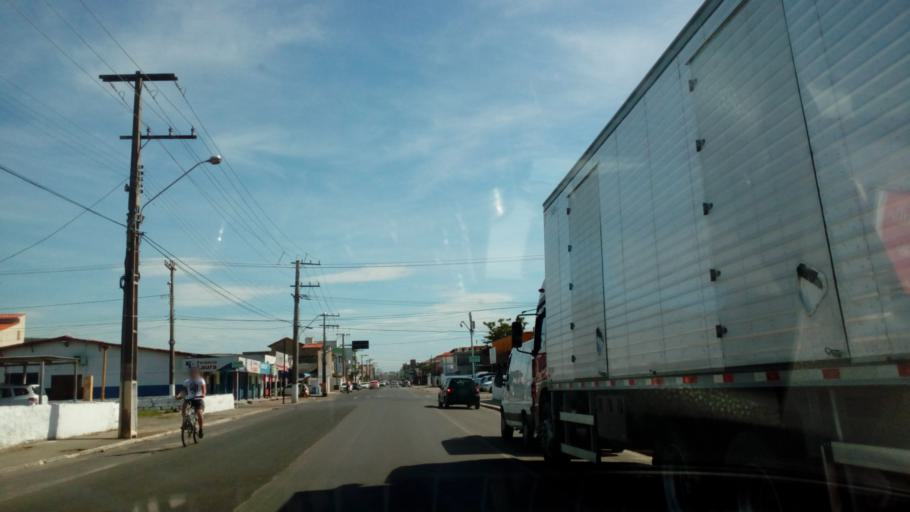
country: BR
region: Santa Catarina
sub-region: Laguna
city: Laguna
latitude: -28.4939
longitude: -48.7730
